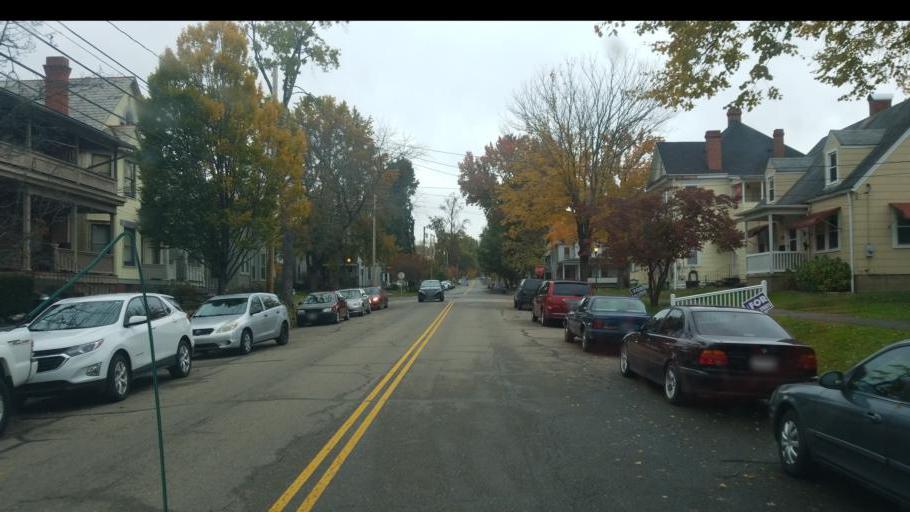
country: US
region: Ohio
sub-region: Washington County
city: Marietta
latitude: 39.4257
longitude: -81.4640
